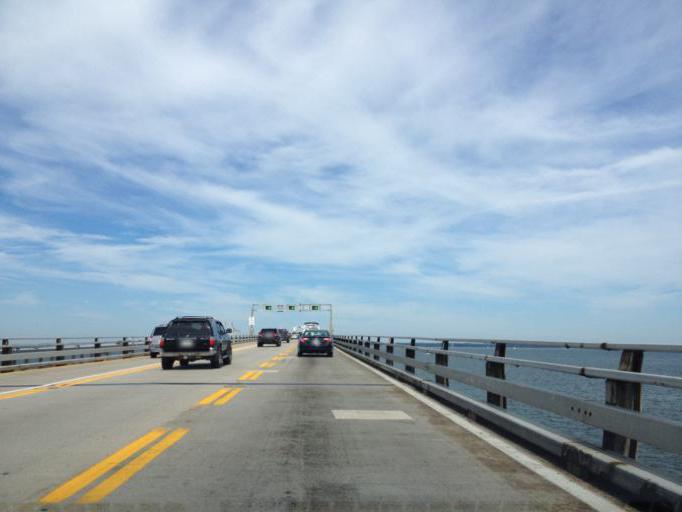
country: US
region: Maryland
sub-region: Queen Anne's County
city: Stevensville
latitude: 38.9865
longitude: -76.3475
